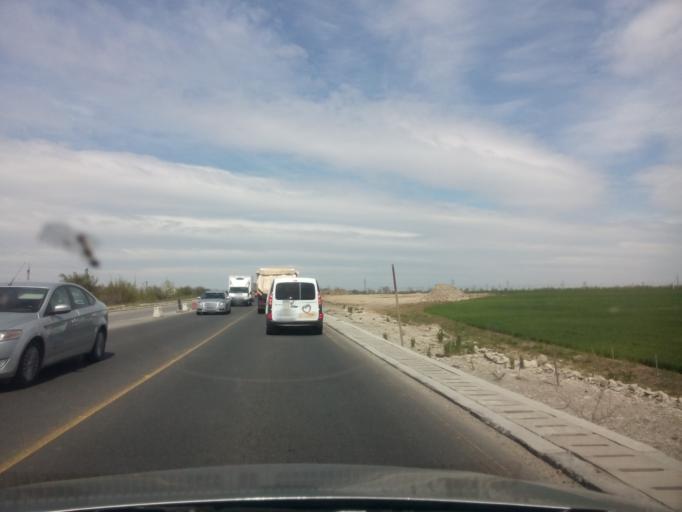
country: RO
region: Ilfov
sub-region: Comuna Pantelimon
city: Pantelimon
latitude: 44.4685
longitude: 26.2325
